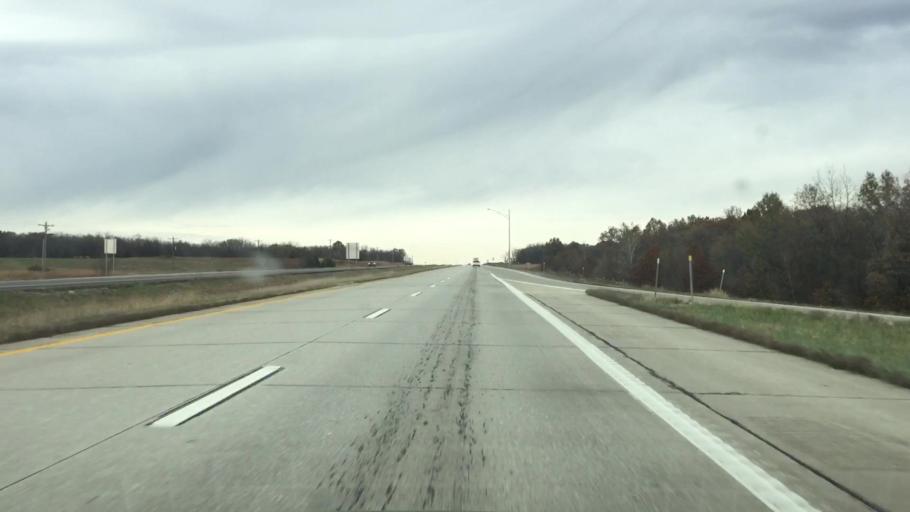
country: US
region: Missouri
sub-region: Saint Clair County
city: Osceola
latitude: 38.0426
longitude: -93.6824
